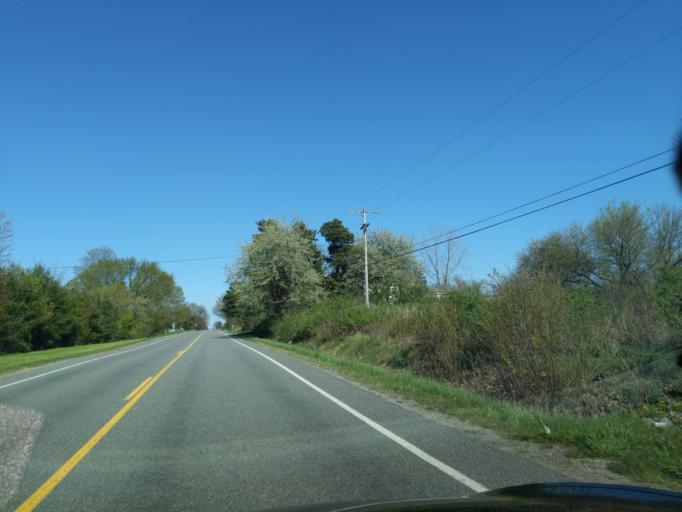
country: US
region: Michigan
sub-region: Kent County
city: Forest Hills
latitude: 42.8852
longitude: -85.4374
